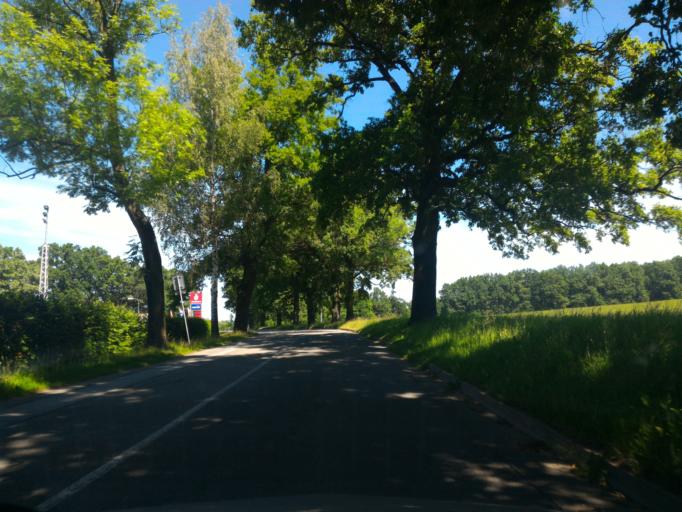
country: CZ
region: Vysocina
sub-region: Okres Jihlava
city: Trest'
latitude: 49.2997
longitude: 15.4829
